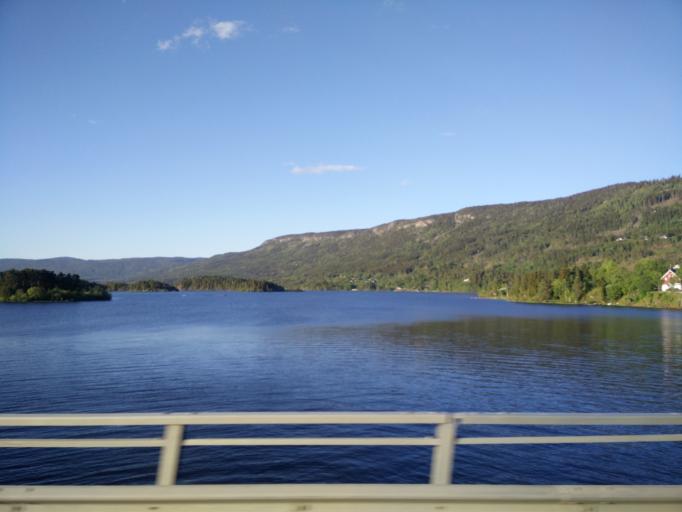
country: NO
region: Buskerud
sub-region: Hole
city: Vik
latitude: 60.0638
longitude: 10.3000
